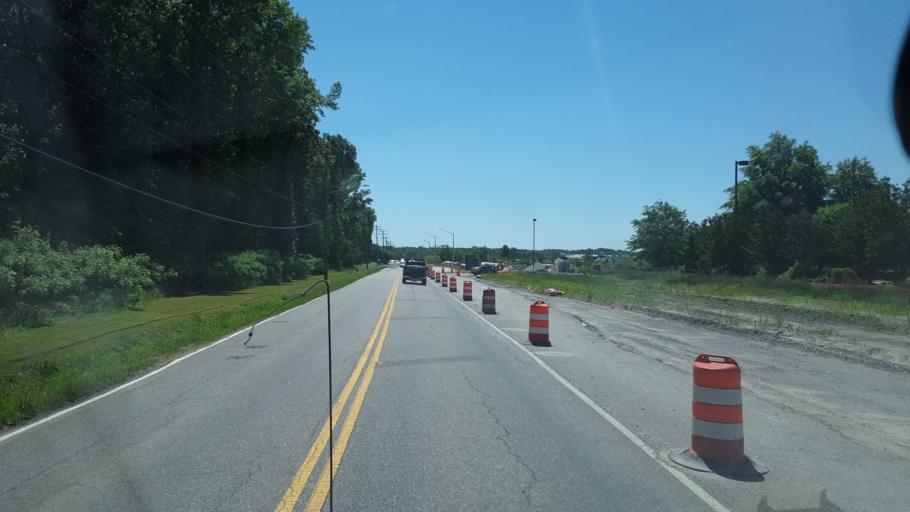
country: US
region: Virginia
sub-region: City of Virginia Beach
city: Virginia Beach
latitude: 36.7504
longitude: -76.0080
